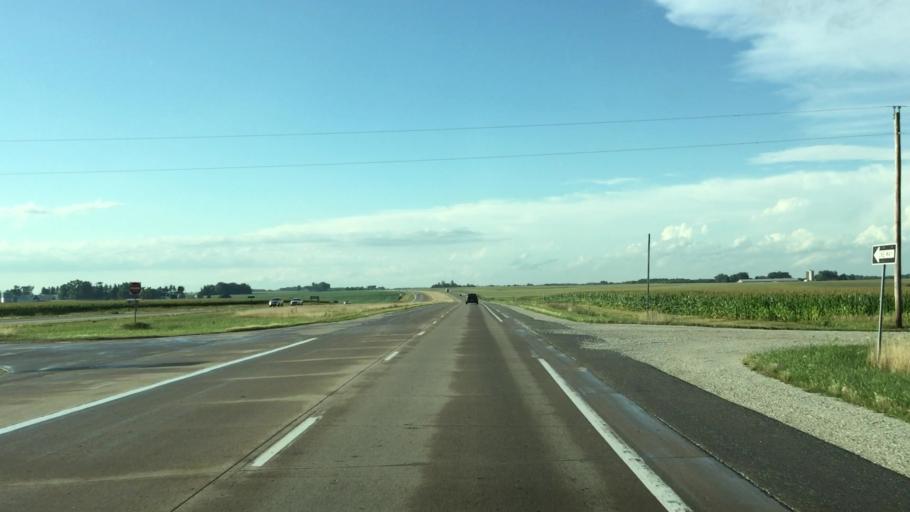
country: US
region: Iowa
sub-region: Henry County
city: Winfield
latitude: 41.1418
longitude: -91.5397
